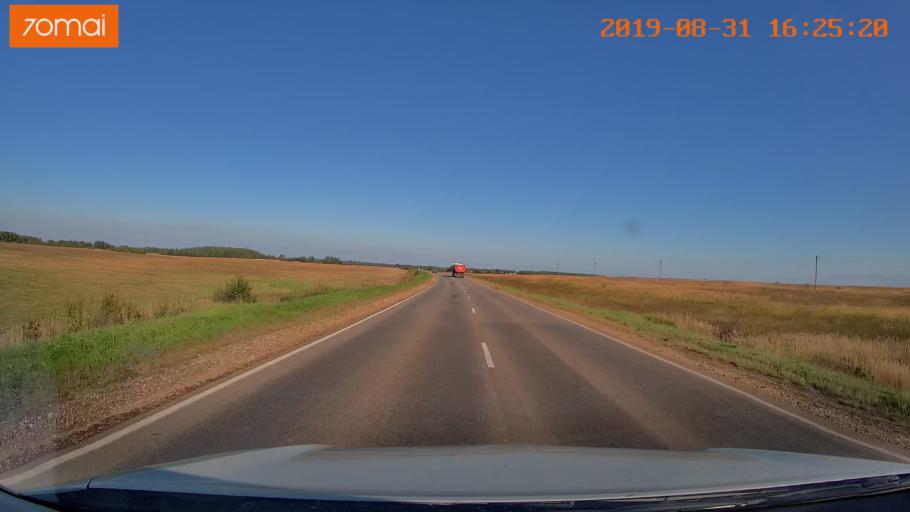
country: RU
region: Kaluga
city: Babynino
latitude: 54.5188
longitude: 35.7108
